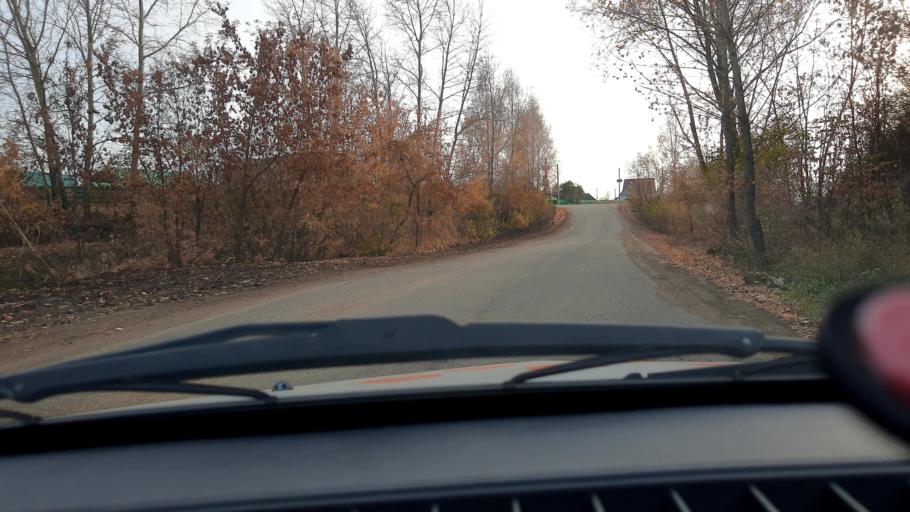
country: RU
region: Bashkortostan
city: Iglino
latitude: 54.7975
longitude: 56.3140
